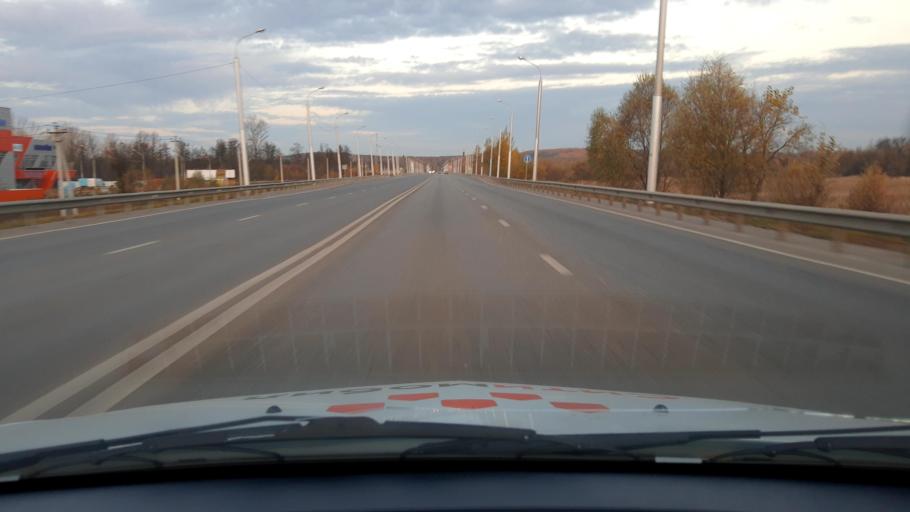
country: RU
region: Bashkortostan
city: Iglino
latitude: 54.8037
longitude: 56.1876
